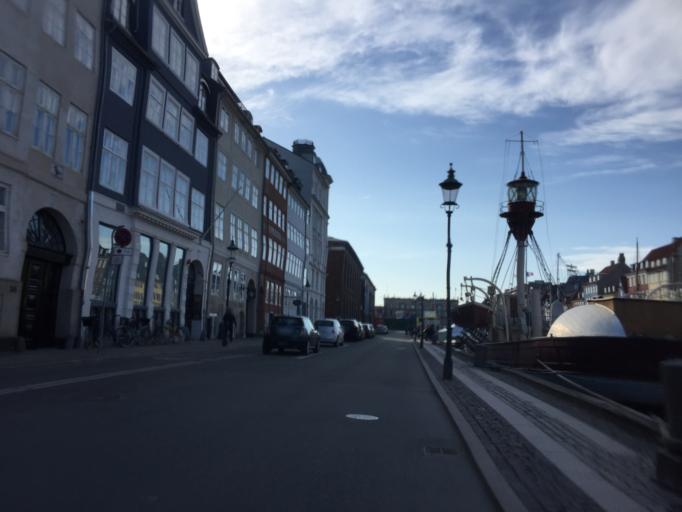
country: DK
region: Capital Region
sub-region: Kobenhavn
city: Christianshavn
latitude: 55.6797
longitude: 12.5902
